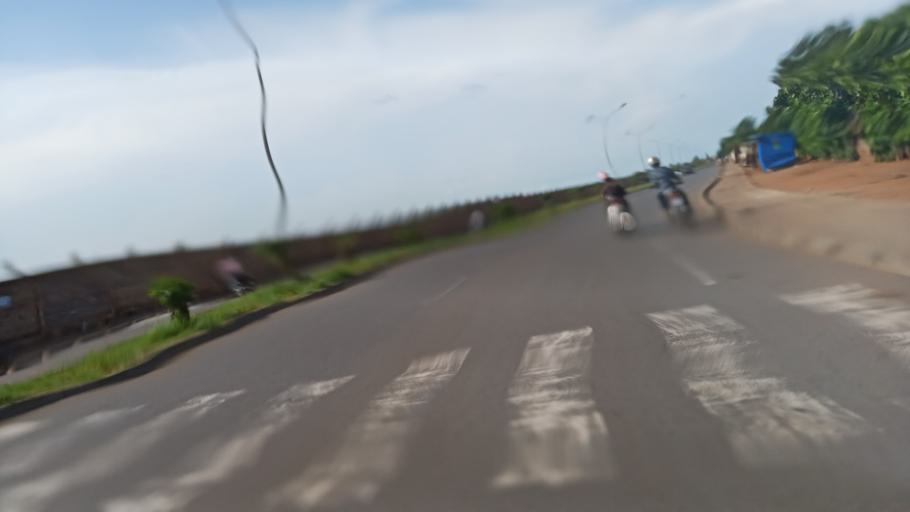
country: TG
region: Maritime
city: Lome
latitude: 6.1791
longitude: 1.2681
